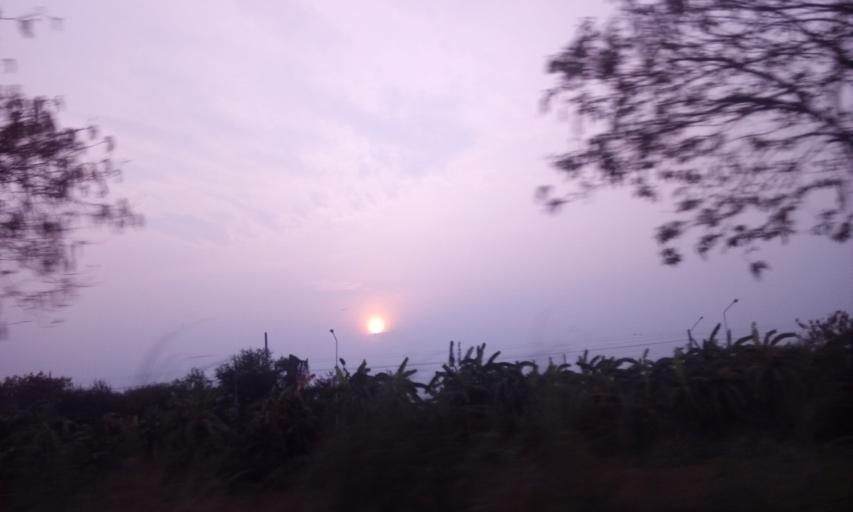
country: TH
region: Bangkok
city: Nong Chok
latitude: 13.9679
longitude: 100.8956
